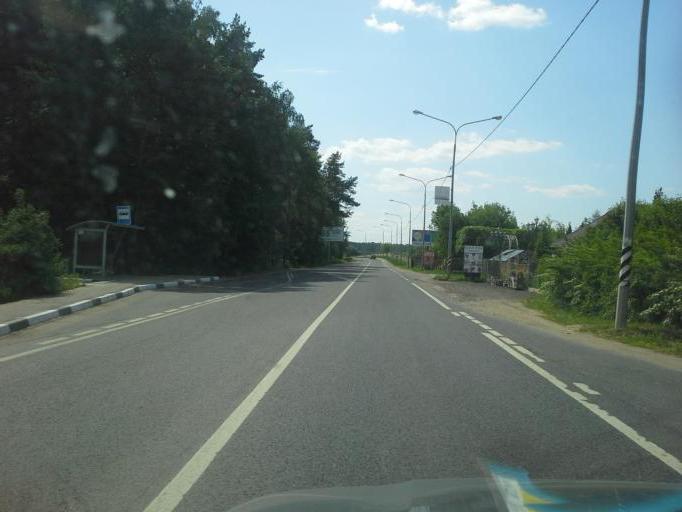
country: RU
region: Moskovskaya
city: Gorki Vtoryye
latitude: 55.7167
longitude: 37.1830
